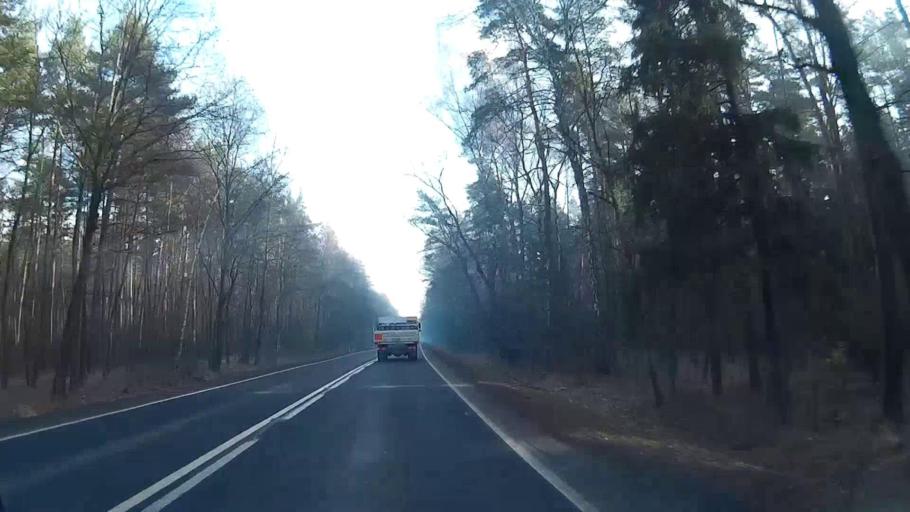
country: PL
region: Lesser Poland Voivodeship
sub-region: Powiat oswiecimski
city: Chelmek
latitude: 50.0771
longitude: 19.2674
